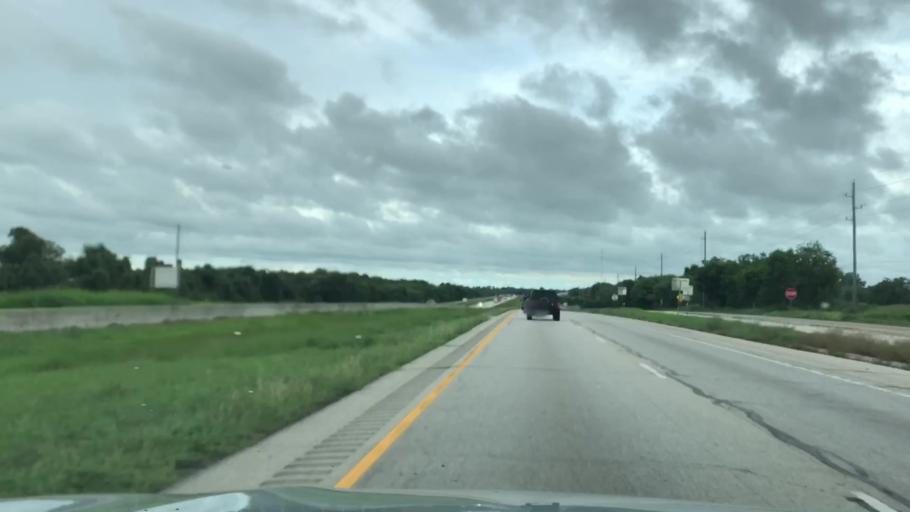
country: US
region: Texas
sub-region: Austin County
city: Sealy
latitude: 29.7719
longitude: -96.0627
